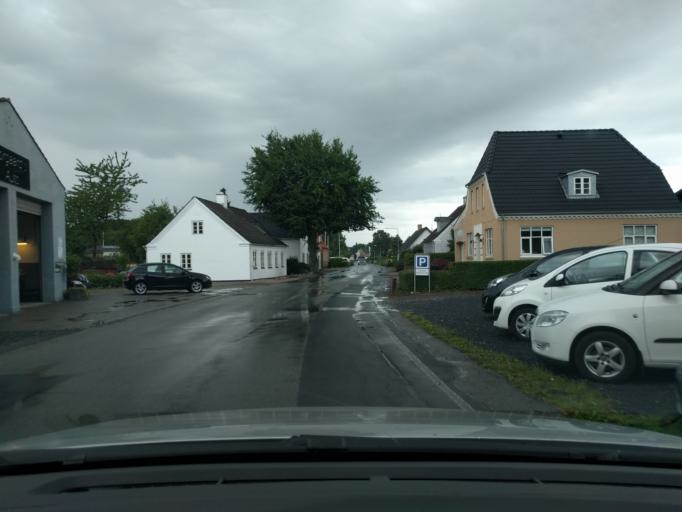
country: DK
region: South Denmark
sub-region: Kerteminde Kommune
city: Langeskov
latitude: 55.3982
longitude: 10.6091
